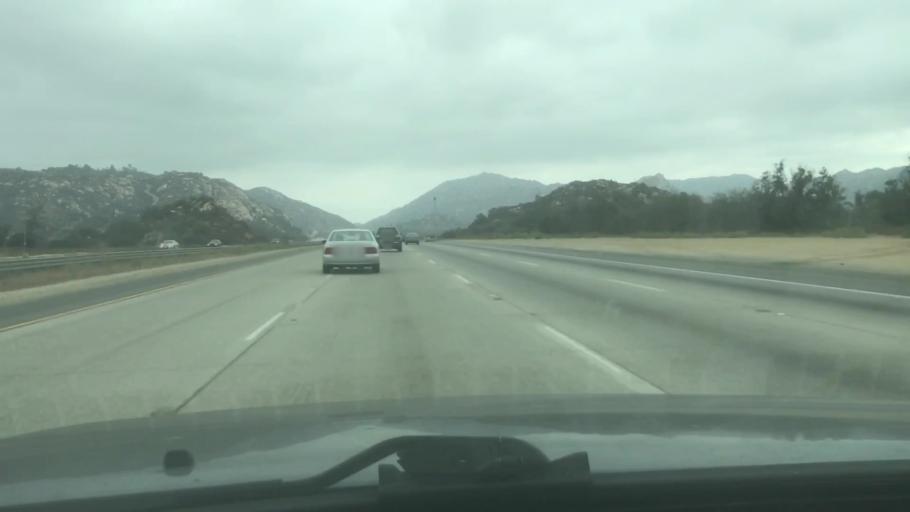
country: US
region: California
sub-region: San Diego County
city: Rainbow
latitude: 33.4053
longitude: -117.1658
